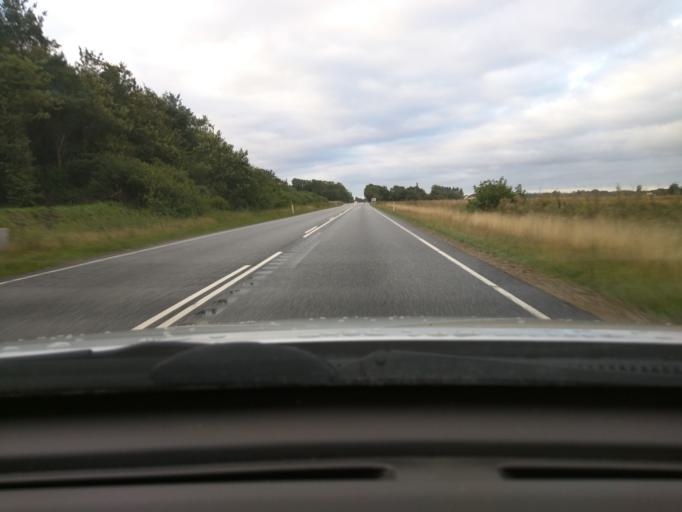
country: DK
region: Central Jutland
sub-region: Silkeborg Kommune
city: Kjellerup
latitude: 56.2923
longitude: 9.3214
